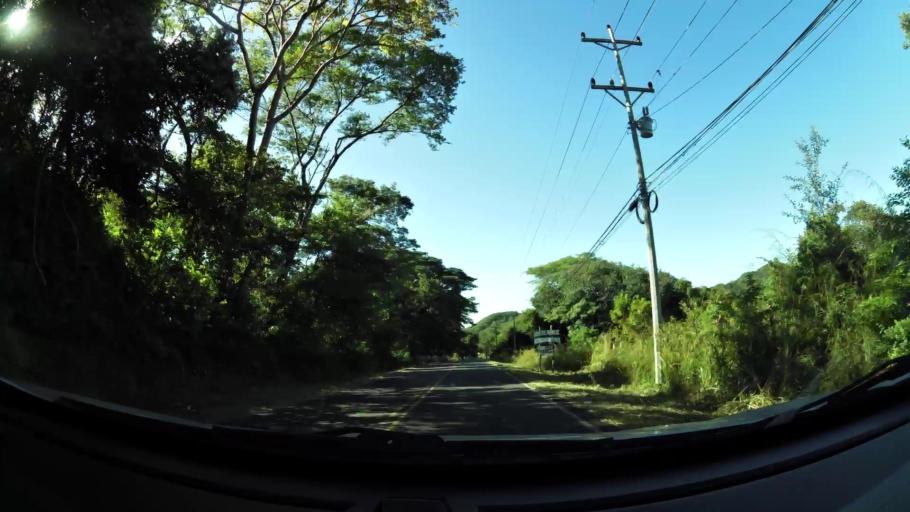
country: CR
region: Guanacaste
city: Belen
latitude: 10.3657
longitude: -85.6451
